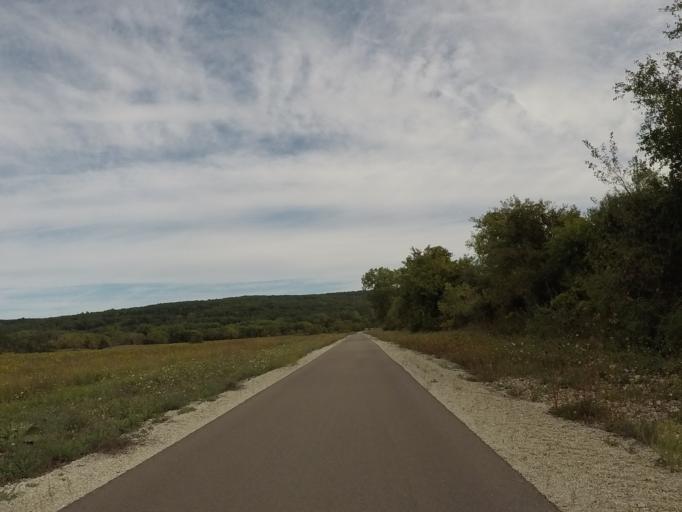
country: US
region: Wisconsin
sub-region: Sauk County
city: Prairie du Sac
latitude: 43.3745
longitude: -89.7355
